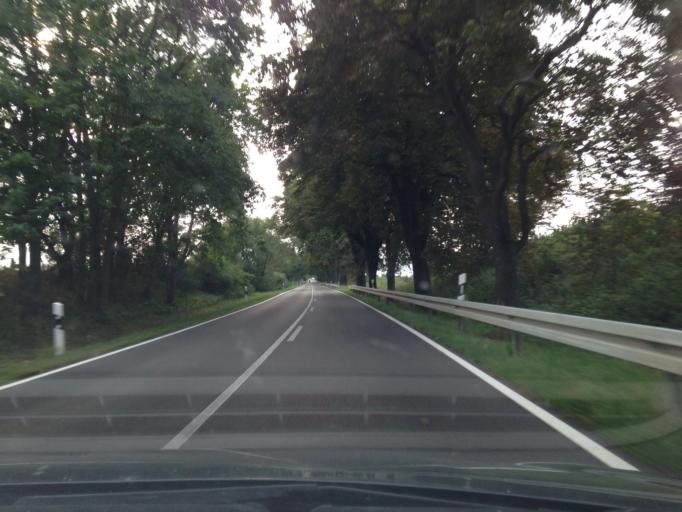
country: DE
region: Mecklenburg-Vorpommern
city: Loitz
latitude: 53.3628
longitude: 13.3967
